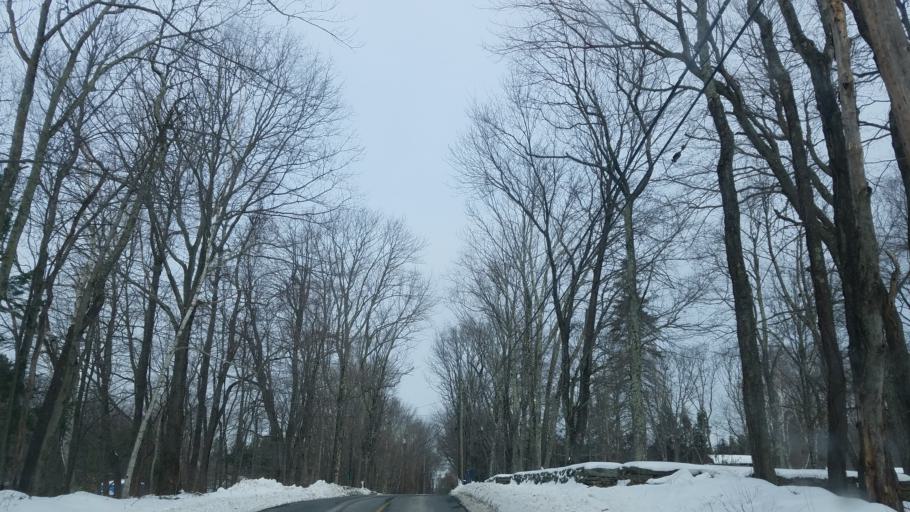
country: US
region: Connecticut
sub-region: Litchfield County
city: New Hartford Center
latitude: 41.8763
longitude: -73.0162
